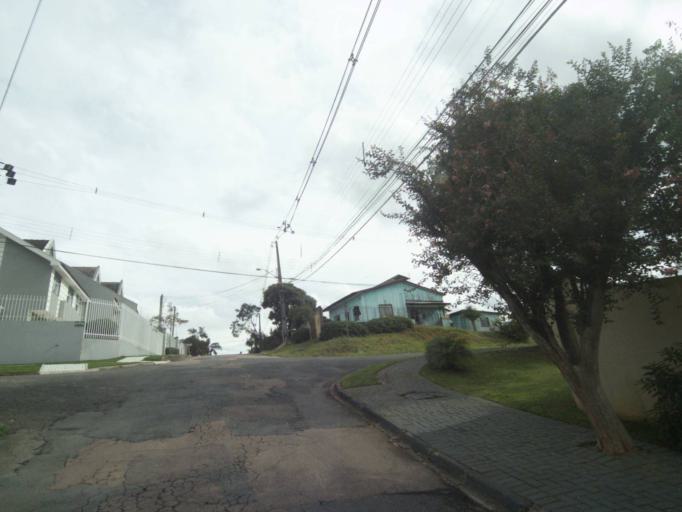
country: BR
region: Parana
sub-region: Curitiba
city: Curitiba
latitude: -25.4403
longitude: -49.3123
